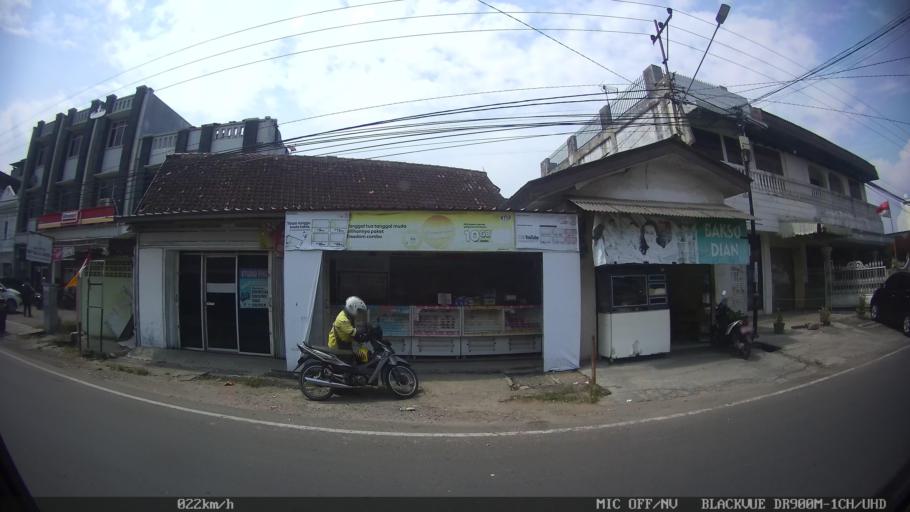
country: ID
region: Lampung
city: Bandarlampung
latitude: -5.4348
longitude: 105.2620
